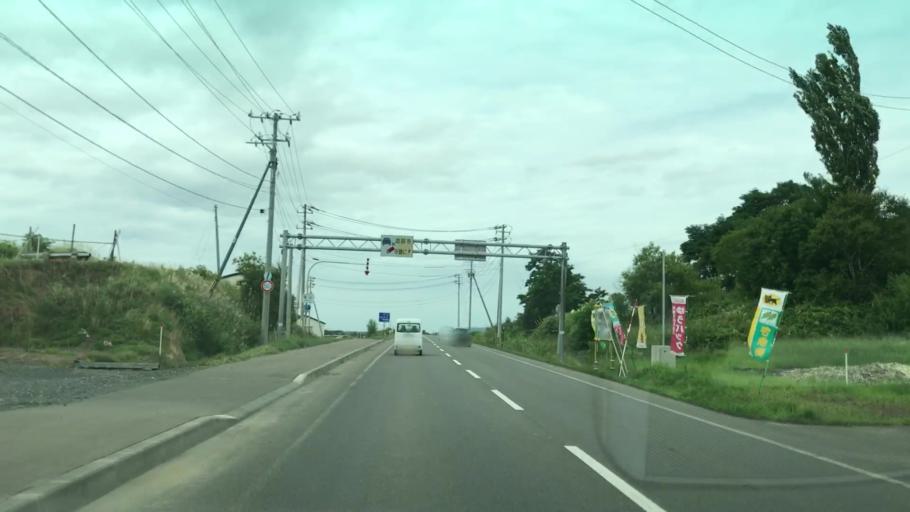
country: JP
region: Hokkaido
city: Iwanai
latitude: 42.9782
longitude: 140.6281
